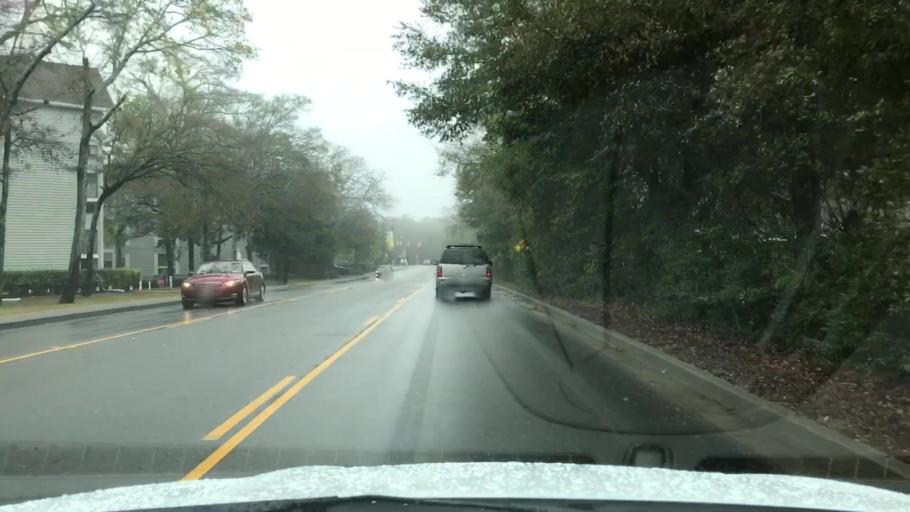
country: US
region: South Carolina
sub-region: Horry County
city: North Myrtle Beach
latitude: 33.7669
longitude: -78.7877
